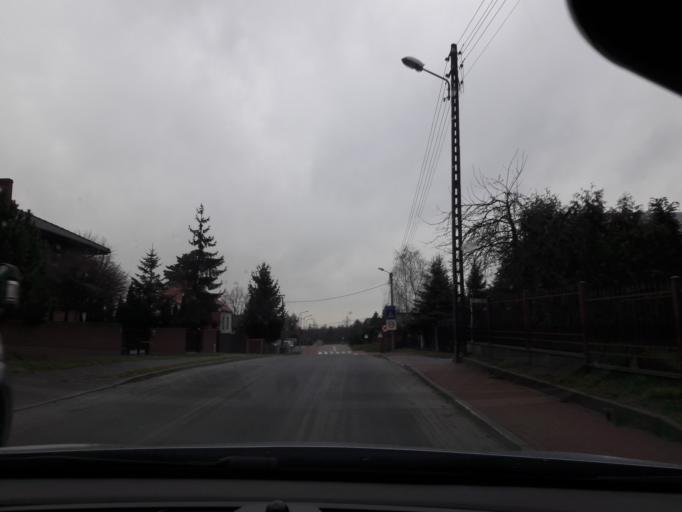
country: PL
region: Greater Poland Voivodeship
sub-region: Powiat poznanski
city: Suchy Las
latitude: 52.4845
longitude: 16.8850
